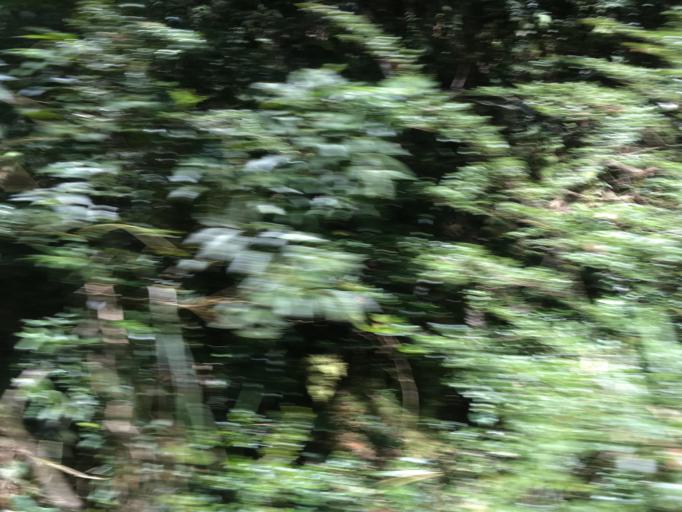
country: TW
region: Taiwan
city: Daxi
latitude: 24.5827
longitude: 121.4131
